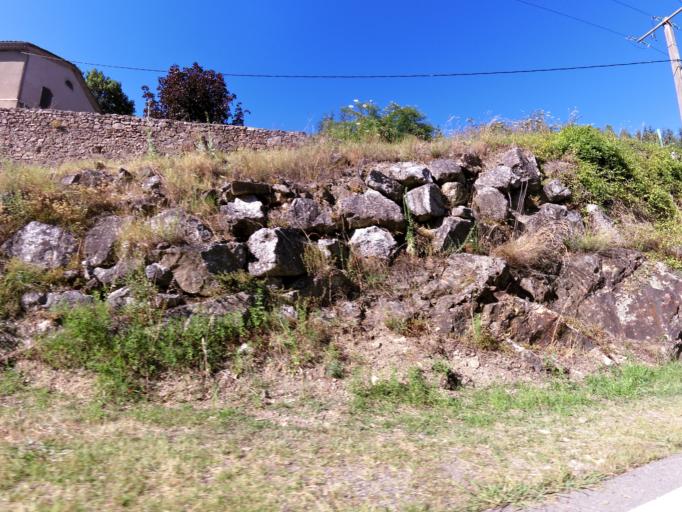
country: FR
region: Languedoc-Roussillon
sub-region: Departement du Gard
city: Saint-Jean-du-Gard
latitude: 44.1125
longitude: 3.8602
